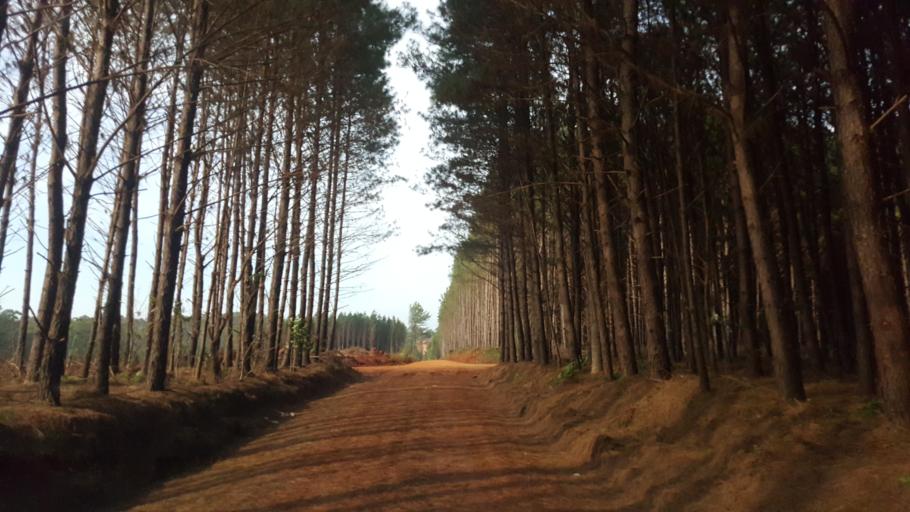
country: AR
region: Misiones
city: Capiovi
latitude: -26.9118
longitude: -55.1167
